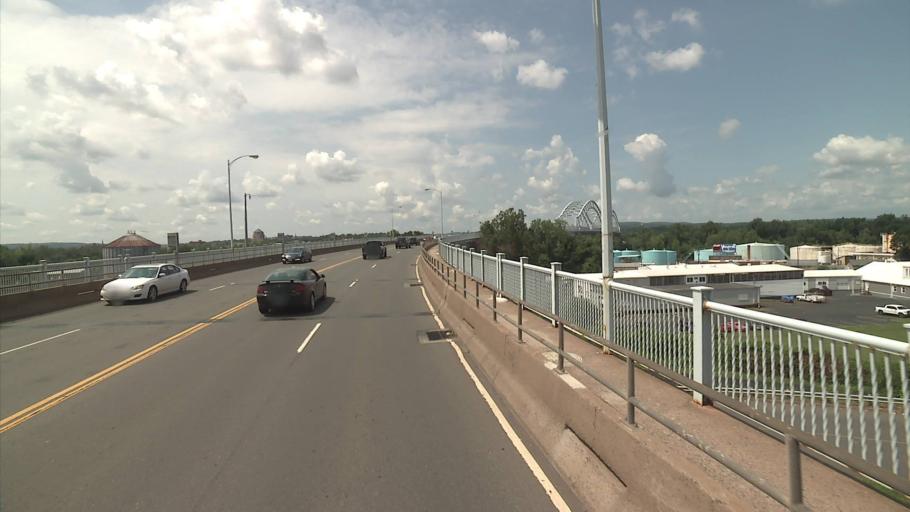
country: US
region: Connecticut
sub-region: Middlesex County
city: Portland
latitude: 41.5708
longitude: -72.6426
